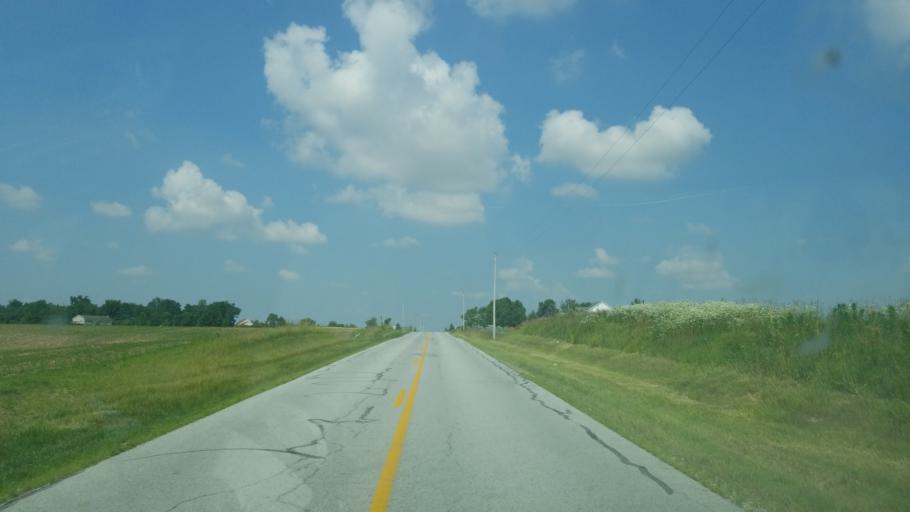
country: US
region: Ohio
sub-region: Shelby County
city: Jackson Center
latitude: 40.5714
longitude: -84.0386
